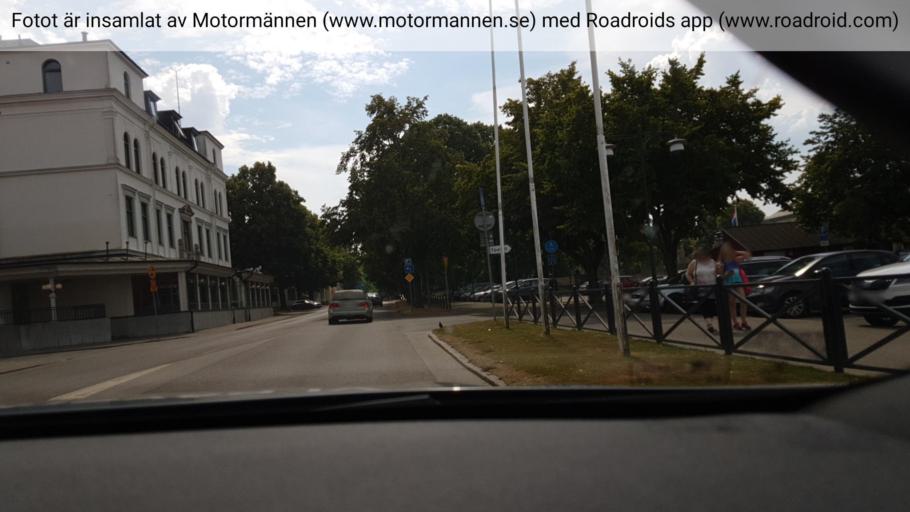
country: SE
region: Vaestra Goetaland
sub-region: Lidkopings Kommun
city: Lidkoping
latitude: 58.5040
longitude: 13.1615
